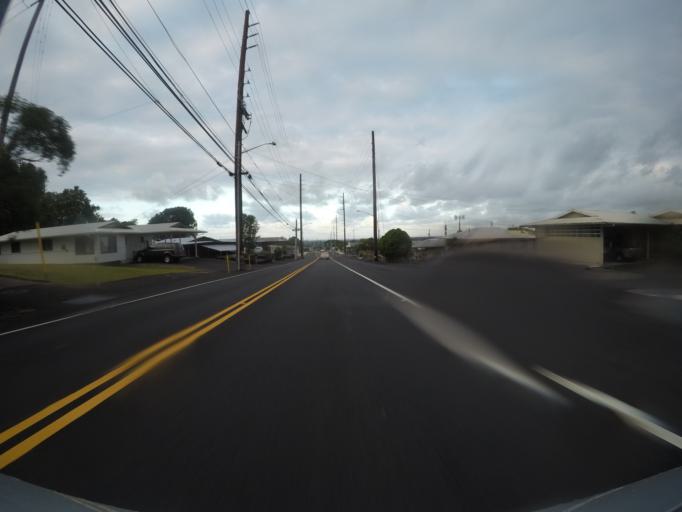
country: US
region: Hawaii
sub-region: Hawaii County
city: Hilo
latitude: 19.6836
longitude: -155.0841
